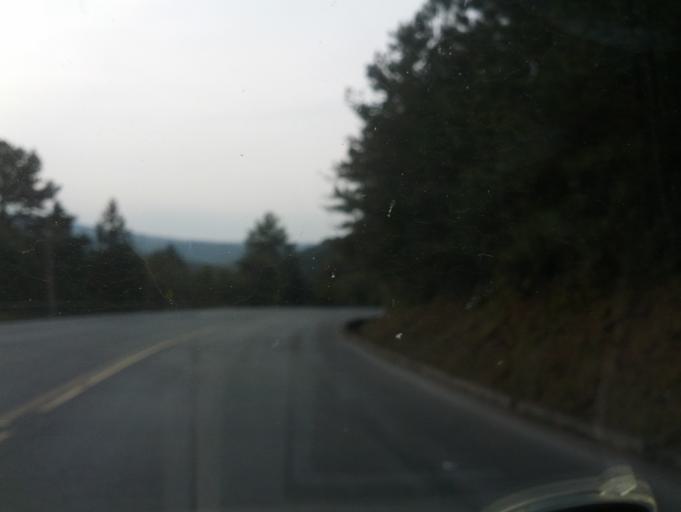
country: BR
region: Santa Catarina
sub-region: Otacilio Costa
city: Otacilio Costa
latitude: -27.2998
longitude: -50.0759
